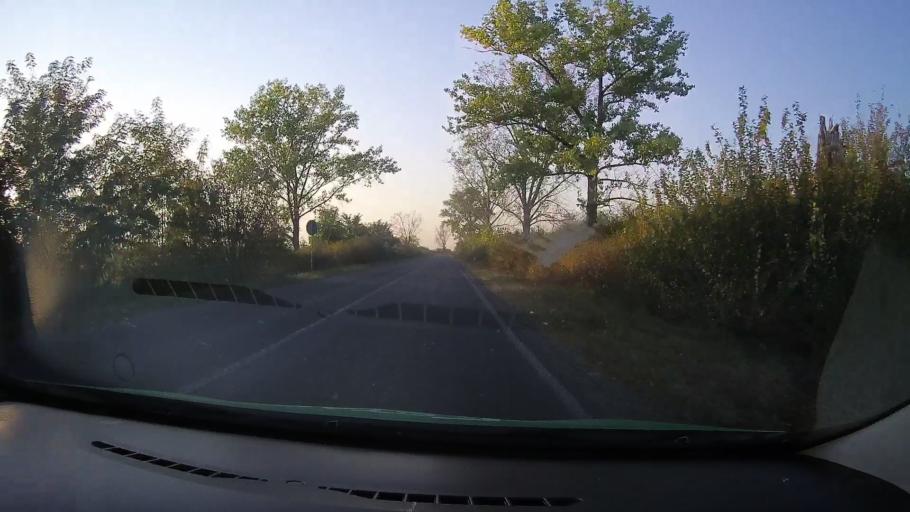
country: RO
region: Arad
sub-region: Comuna Bocsig
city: Bocsig
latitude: 46.4265
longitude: 21.9099
